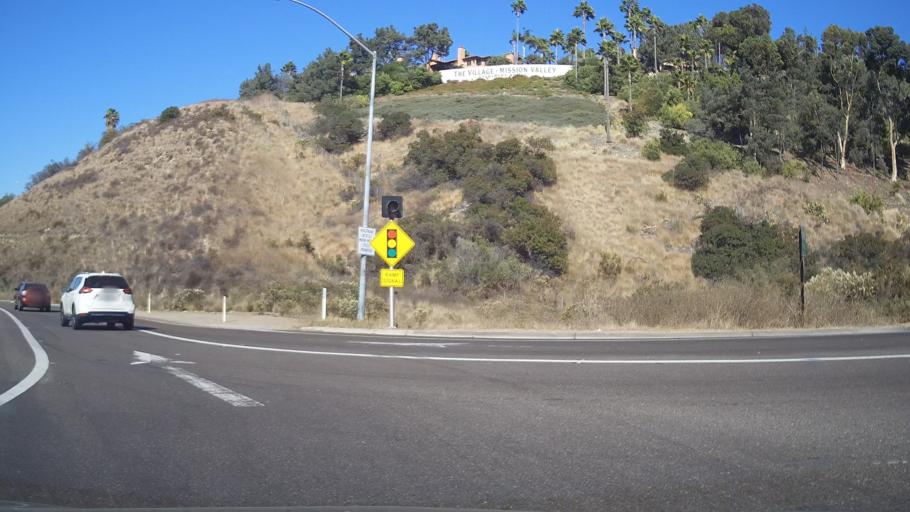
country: US
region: California
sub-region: San Diego County
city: San Diego
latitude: 32.7888
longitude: -117.1120
